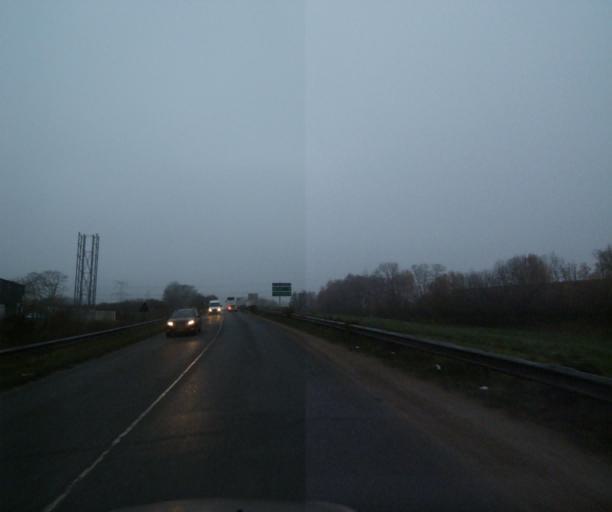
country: FR
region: Ile-de-France
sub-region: Departement de Seine-et-Marne
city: Saint-Thibault-des-Vignes
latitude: 48.8611
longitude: 2.6707
